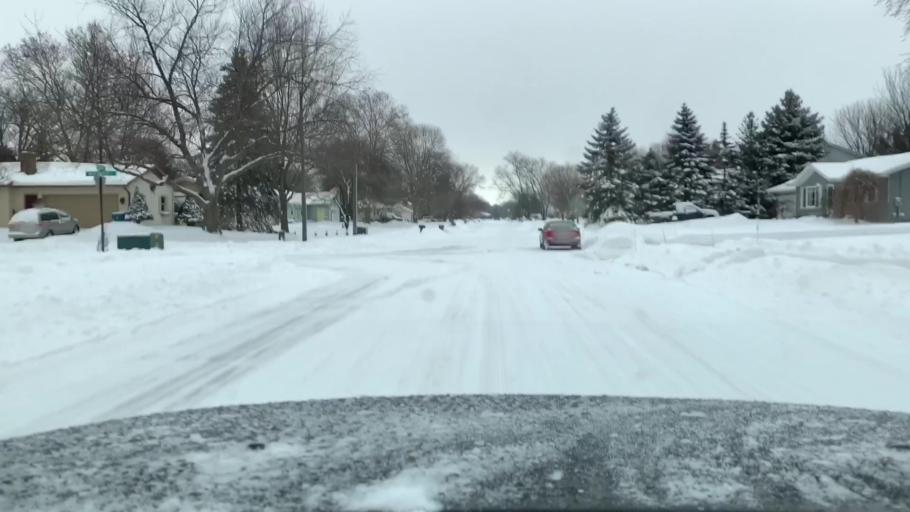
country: US
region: Michigan
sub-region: Ottawa County
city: Zeeland
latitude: 42.8063
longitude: -86.0281
